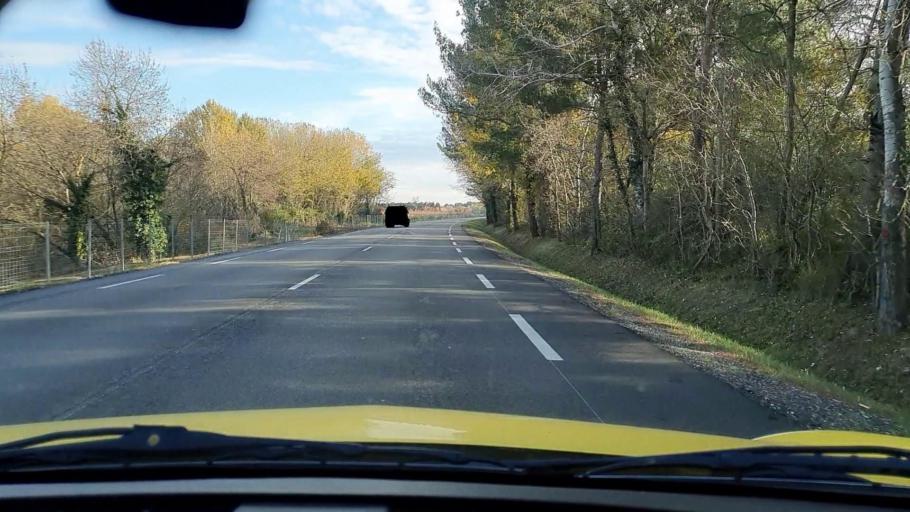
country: FR
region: Languedoc-Roussillon
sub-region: Departement du Gard
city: Vallabregues
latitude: 43.8711
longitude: 4.6317
